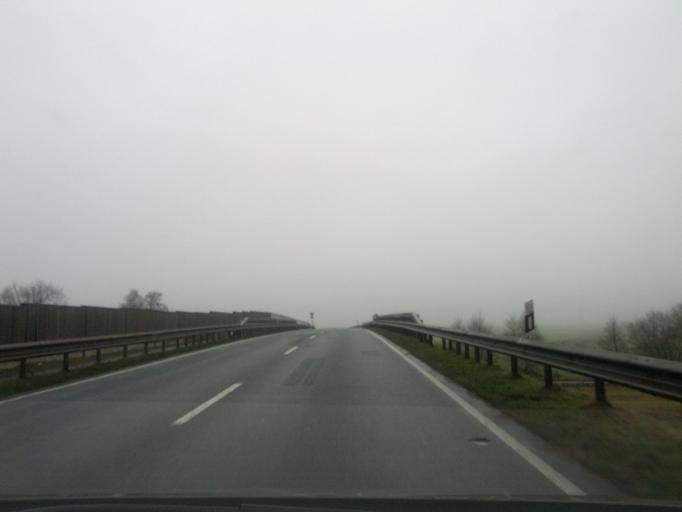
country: DE
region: Lower Saxony
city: Nottensdorf
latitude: 53.4974
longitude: 9.5967
